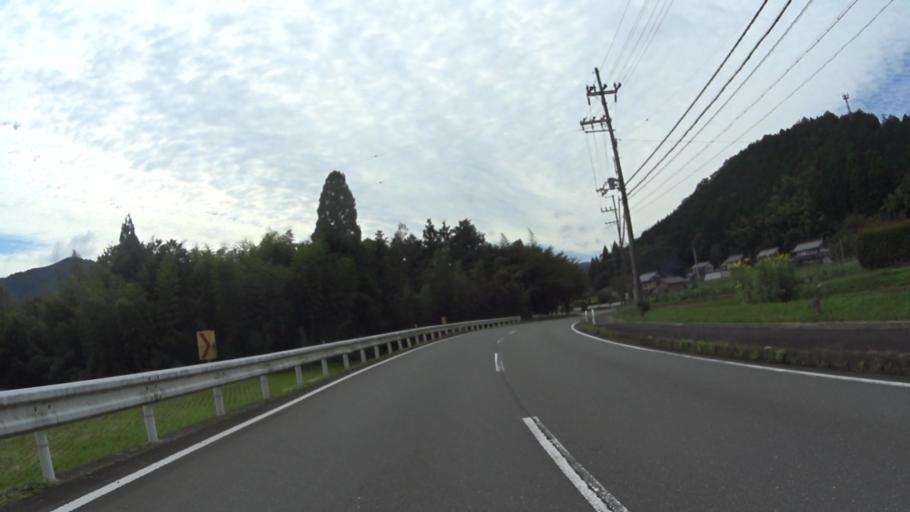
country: JP
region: Kyoto
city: Ayabe
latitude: 35.2557
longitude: 135.4247
